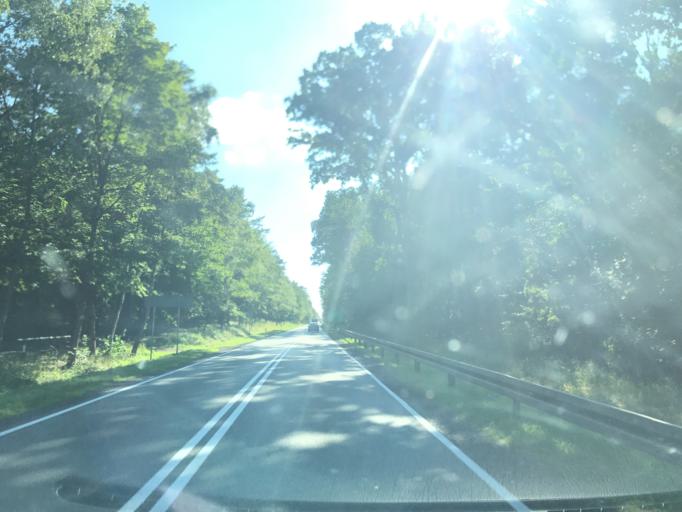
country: PL
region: Kujawsko-Pomorskie
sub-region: Wloclawek
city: Wloclawek
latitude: 52.6337
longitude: 19.0223
